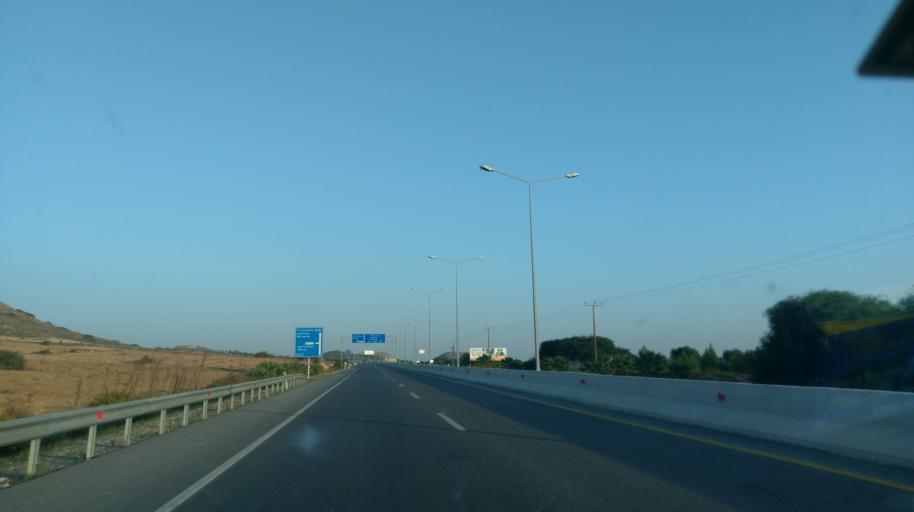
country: CY
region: Lefkosia
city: Akaki
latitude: 35.1954
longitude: 33.1053
